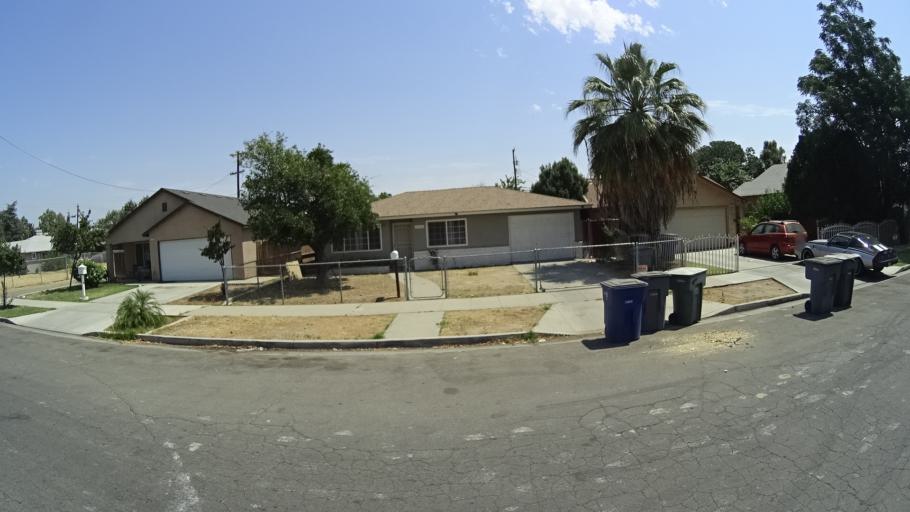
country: US
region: California
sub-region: Fresno County
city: Fresno
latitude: 36.7276
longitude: -119.8027
